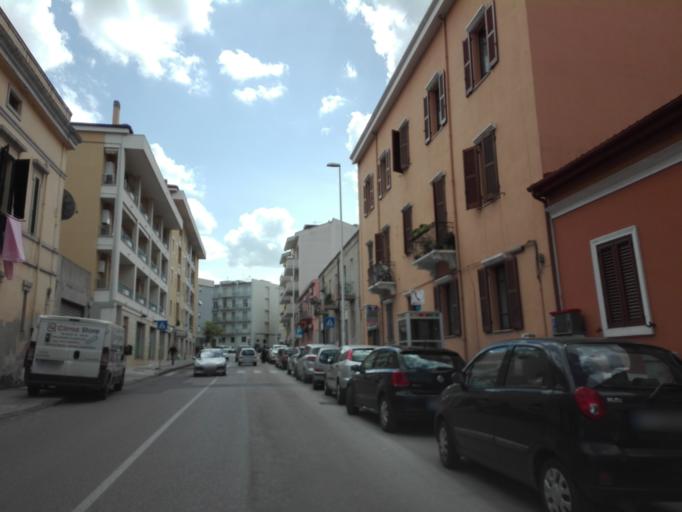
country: IT
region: Sardinia
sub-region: Provincia di Sassari
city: Sassari
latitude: 40.7333
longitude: 8.5567
